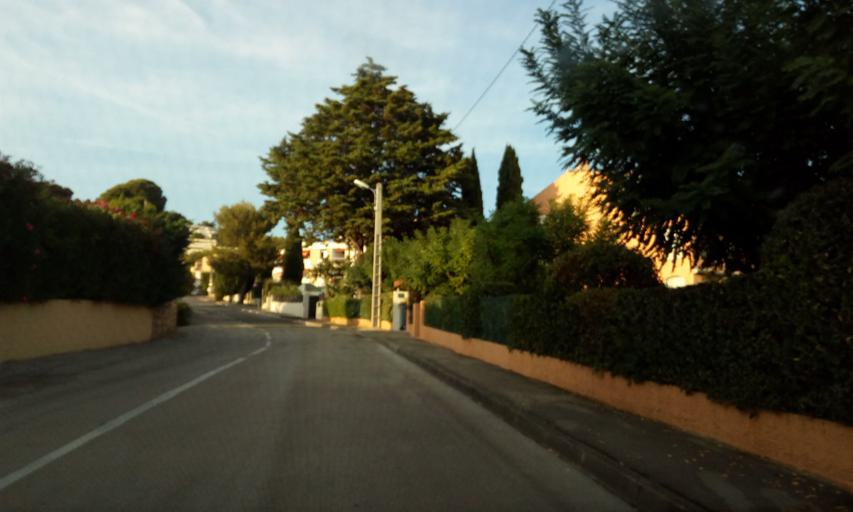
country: FR
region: Provence-Alpes-Cote d'Azur
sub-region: Departement du Var
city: Bandol
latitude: 43.1406
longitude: 5.7578
